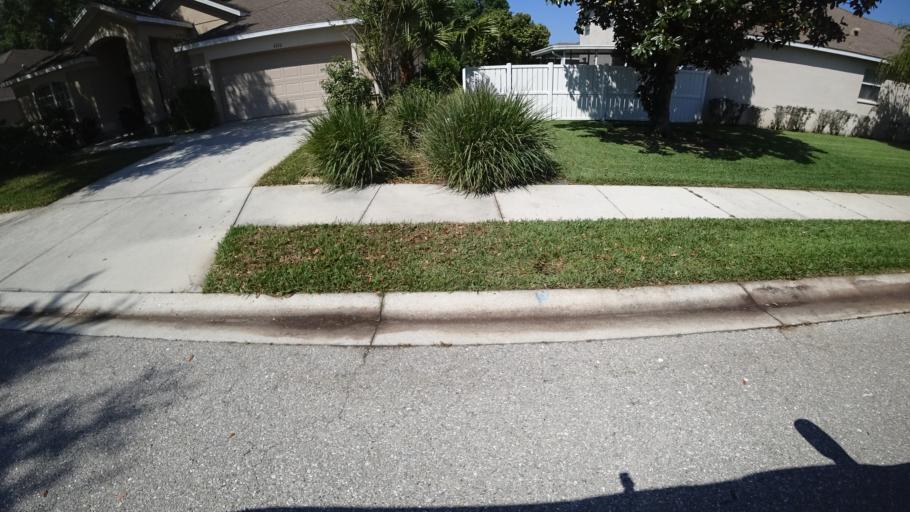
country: US
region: Florida
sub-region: Manatee County
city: Samoset
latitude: 27.4631
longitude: -82.5224
